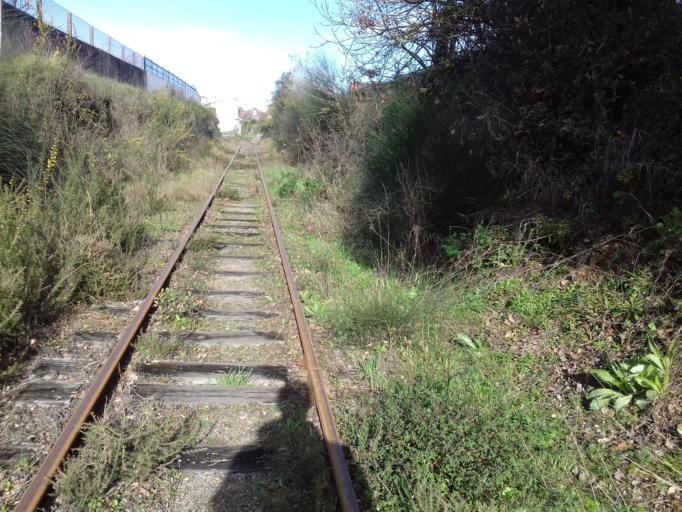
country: PT
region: Aveiro
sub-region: Albergaria-A-Velha
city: Branca
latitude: 40.7705
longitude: -8.4836
